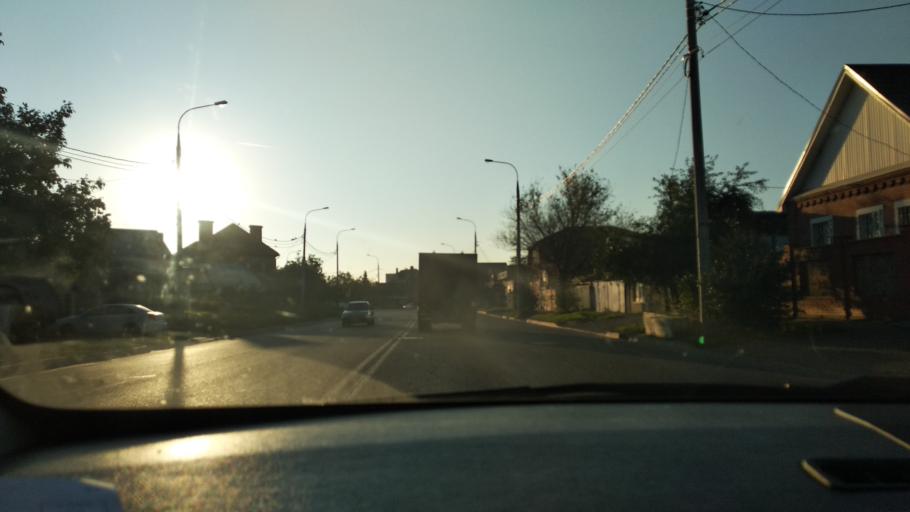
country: RU
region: Krasnodarskiy
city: Krasnodar
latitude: 45.0119
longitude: 39.0085
